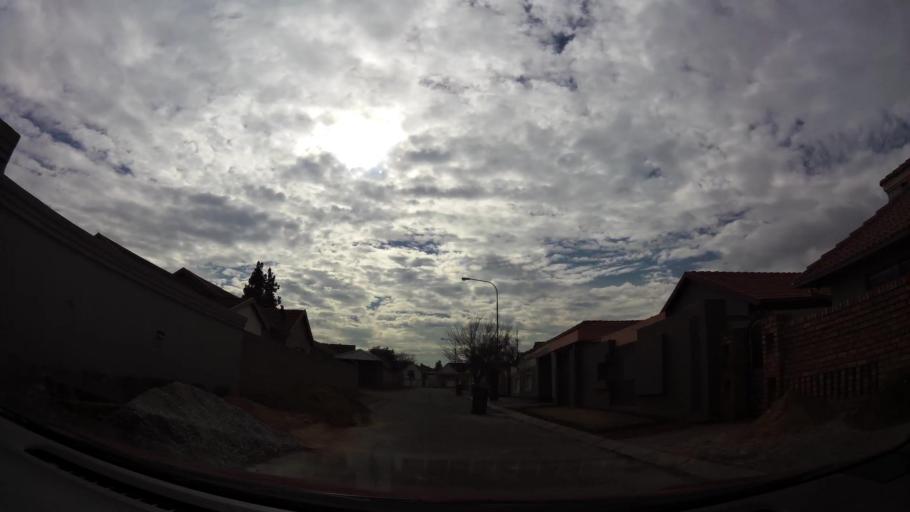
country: ZA
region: Gauteng
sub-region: City of Johannesburg Metropolitan Municipality
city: Soweto
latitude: -26.2769
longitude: 27.8321
